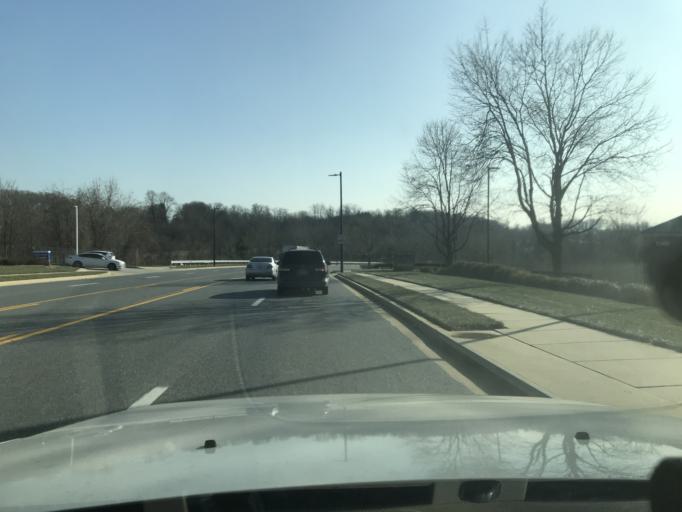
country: US
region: Maryland
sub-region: Baltimore County
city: Owings Mills
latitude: 39.4236
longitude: -76.8056
